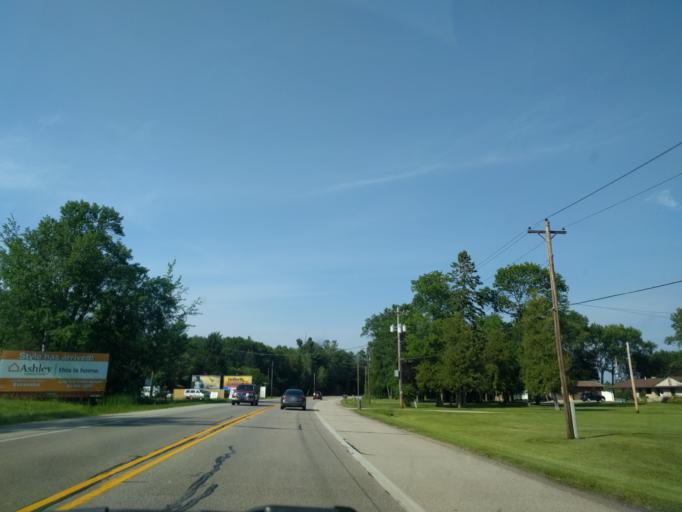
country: US
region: Michigan
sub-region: Delta County
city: Escanaba
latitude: 45.7050
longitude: -87.1005
